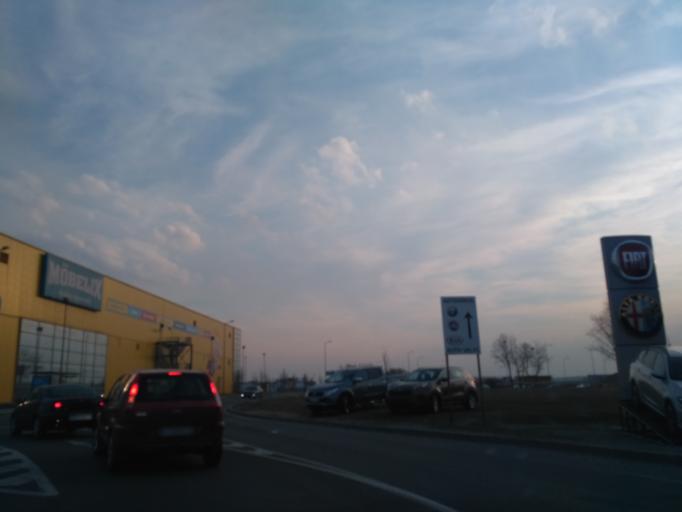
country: SK
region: Kosicky
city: Kosice
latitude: 48.6988
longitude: 21.2496
